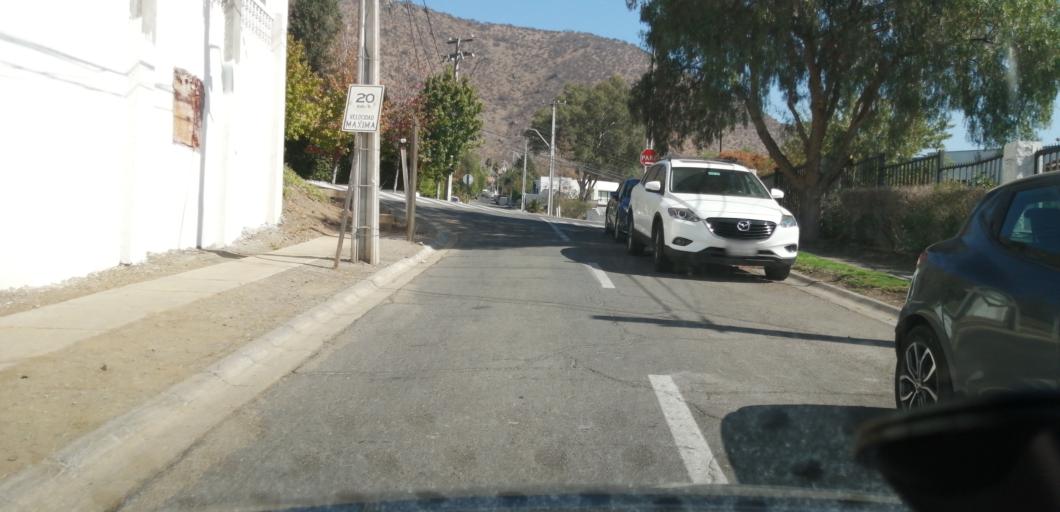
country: CL
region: Santiago Metropolitan
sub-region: Provincia de Santiago
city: Lo Prado
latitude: -33.4571
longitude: -70.8206
